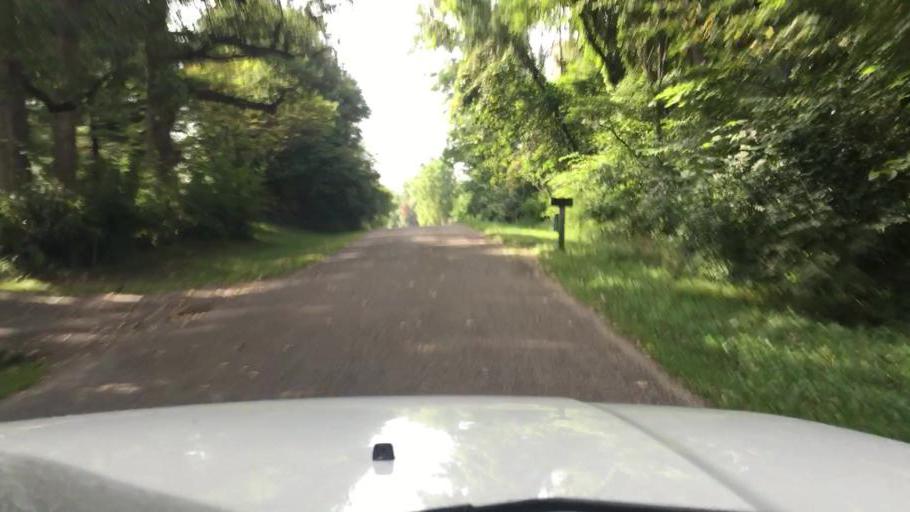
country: US
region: Ohio
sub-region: Champaign County
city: Mechanicsburg
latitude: 40.0662
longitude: -83.6023
